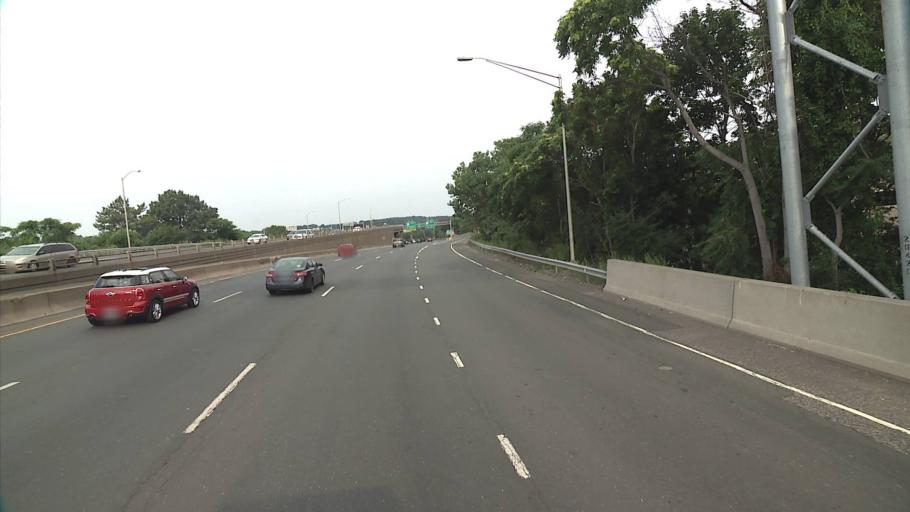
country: US
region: Connecticut
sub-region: New Haven County
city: Waterbury
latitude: 41.5514
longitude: -73.0395
